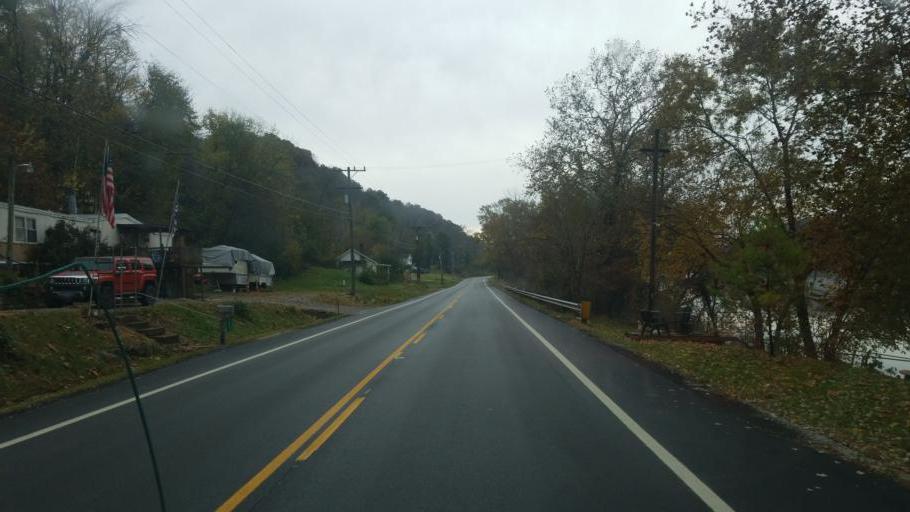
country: US
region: Ohio
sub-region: Washington County
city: Beverly
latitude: 39.5639
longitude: -81.5714
